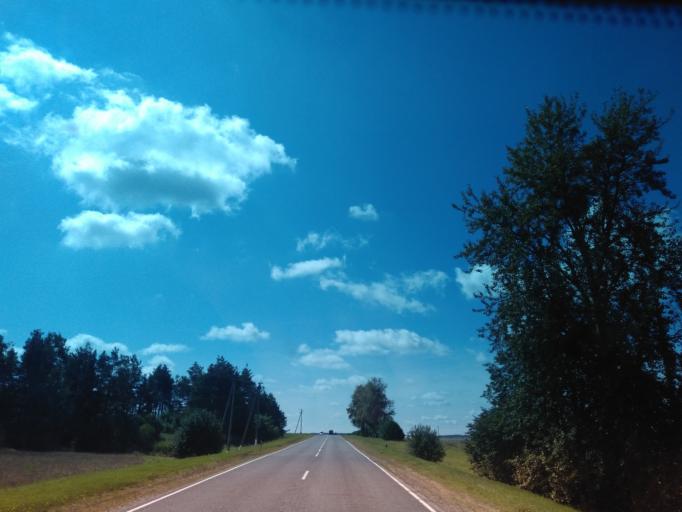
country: BY
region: Minsk
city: Uzda
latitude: 53.3827
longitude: 27.2407
